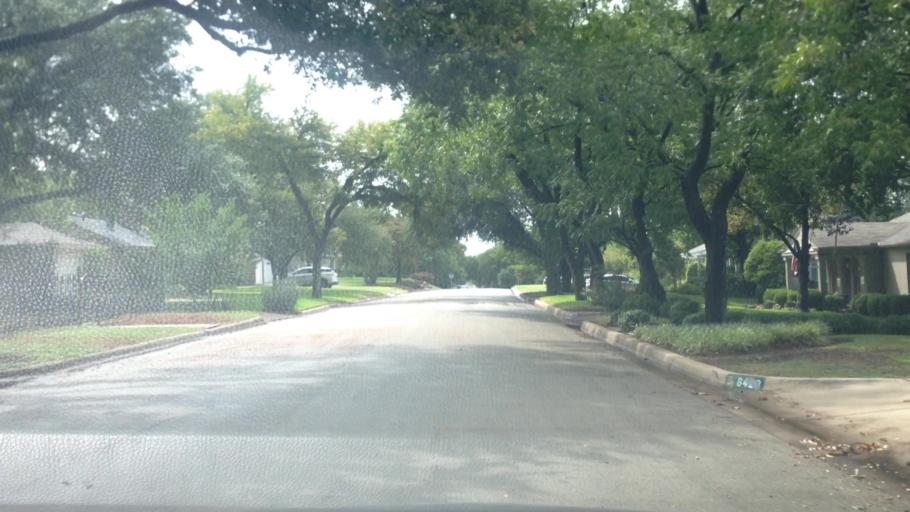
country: US
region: Texas
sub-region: Tarrant County
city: Westworth
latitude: 32.7334
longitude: -97.4258
